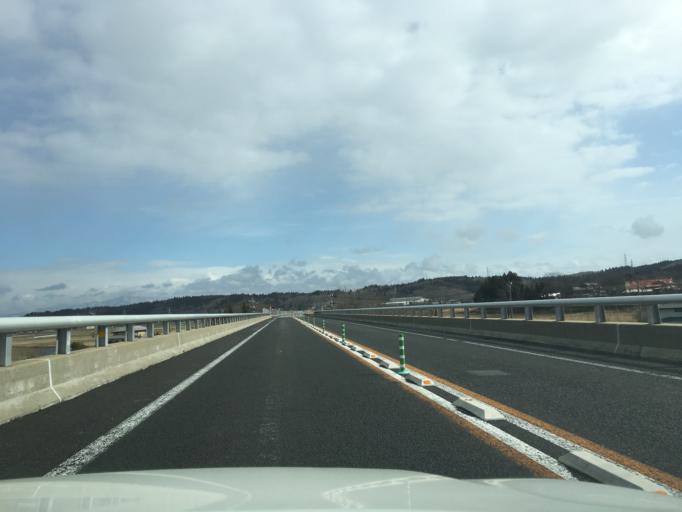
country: JP
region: Akita
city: Akita
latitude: 39.6218
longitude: 140.1520
